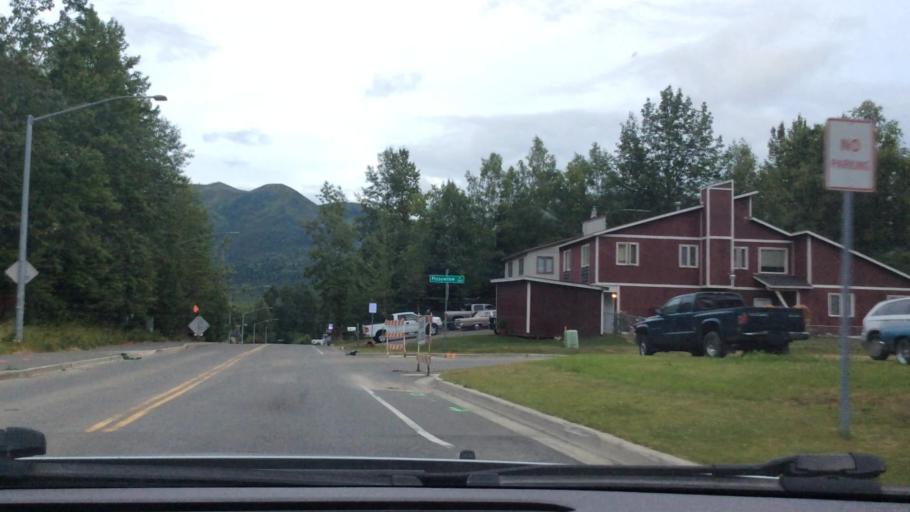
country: US
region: Alaska
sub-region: Anchorage Municipality
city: Elmendorf Air Force Base
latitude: 61.1919
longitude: -149.7265
